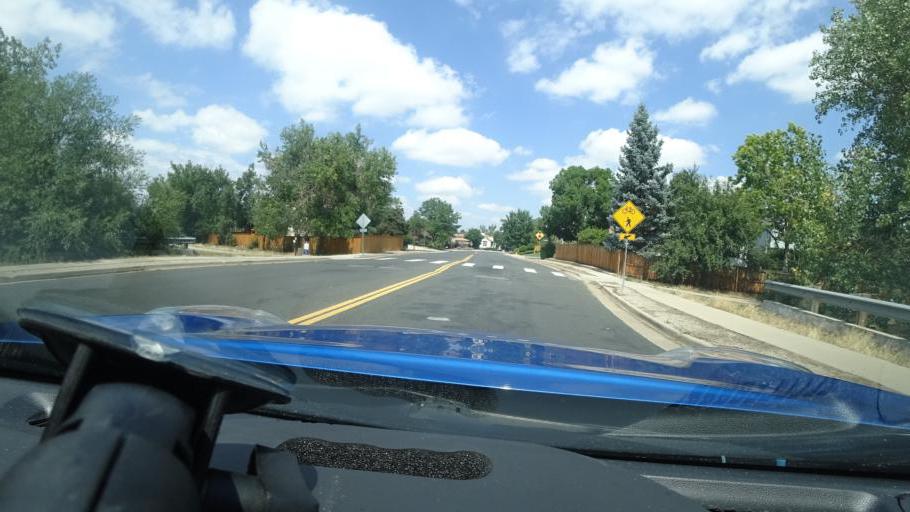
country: US
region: Colorado
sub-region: Adams County
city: Aurora
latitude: 39.7149
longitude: -104.8556
